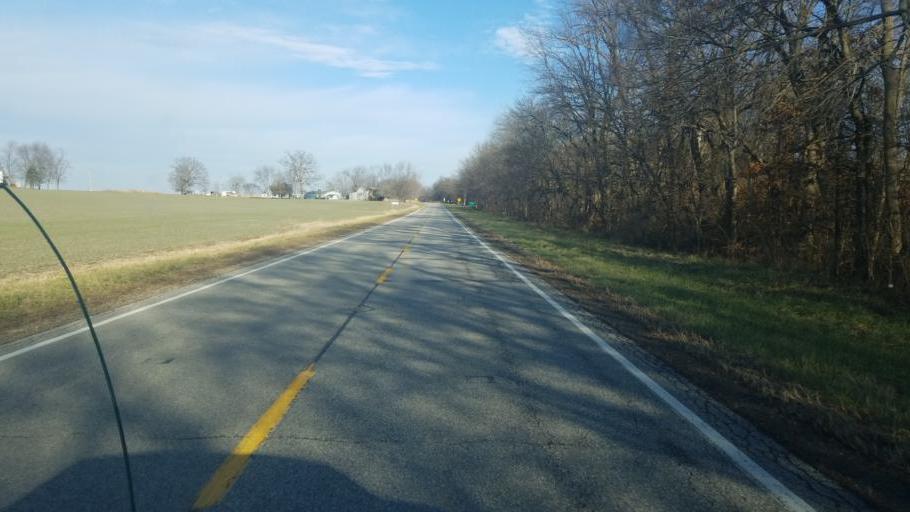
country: US
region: Illinois
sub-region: Wabash County
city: Mount Carmel
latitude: 38.3477
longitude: -87.8753
